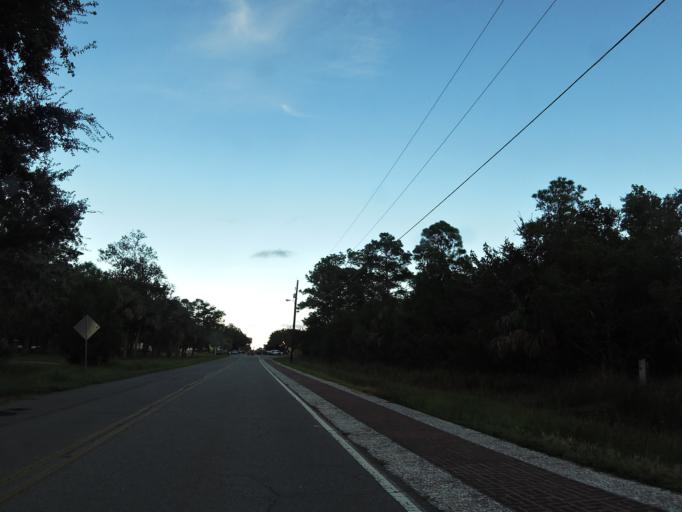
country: US
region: Georgia
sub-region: Camden County
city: St. Marys
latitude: 30.7214
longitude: -81.5548
